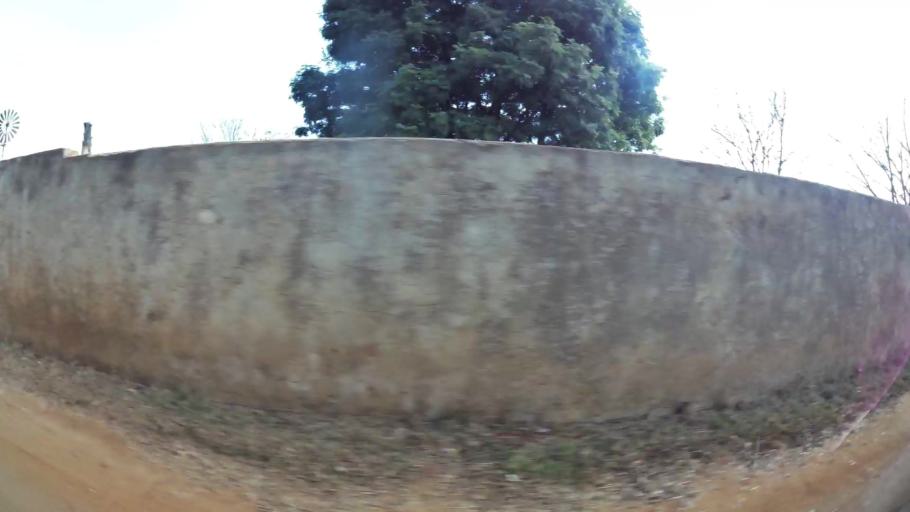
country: ZA
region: Gauteng
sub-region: Ekurhuleni Metropolitan Municipality
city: Benoni
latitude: -26.0891
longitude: 28.3648
